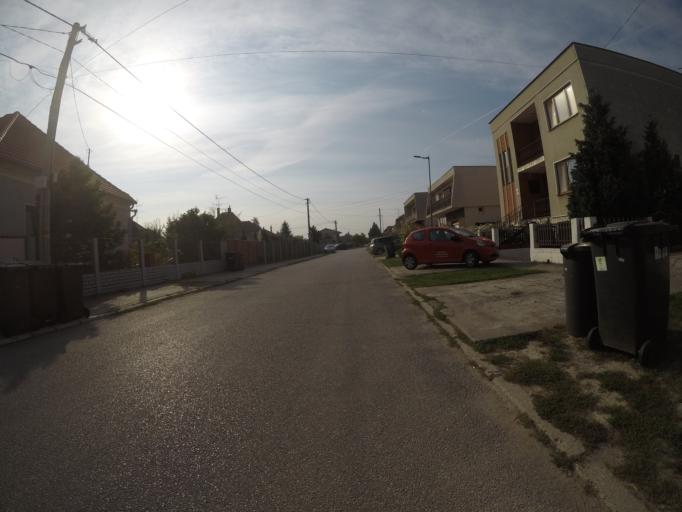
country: SK
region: Trnavsky
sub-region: Okres Dunajska Streda
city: Velky Meder
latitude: 47.8537
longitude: 17.7616
